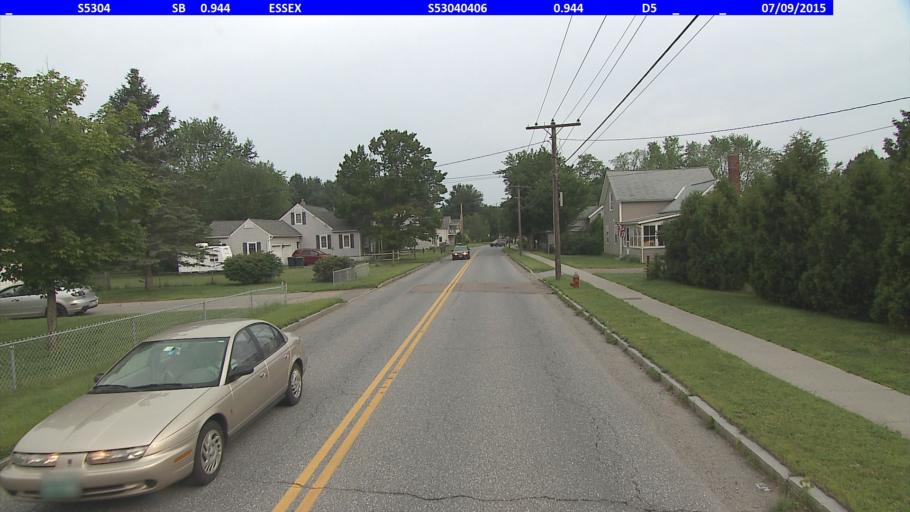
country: US
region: Vermont
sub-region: Chittenden County
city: Essex Junction
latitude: 44.4878
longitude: -73.1216
